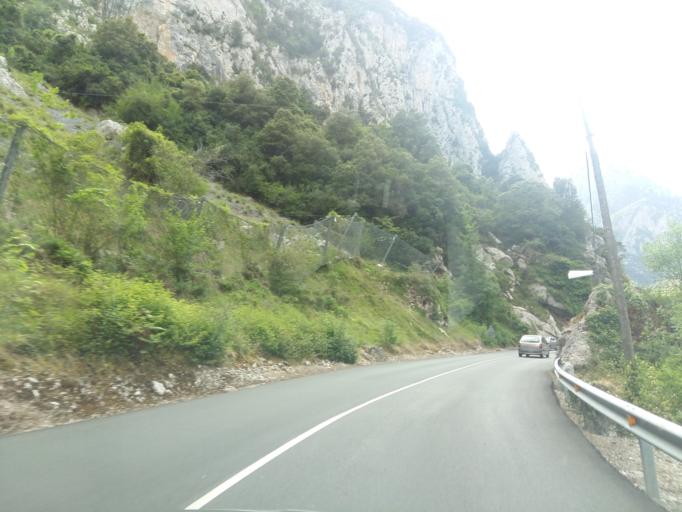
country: ES
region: Cantabria
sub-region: Provincia de Cantabria
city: Tresviso
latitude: 43.2492
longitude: -4.5988
